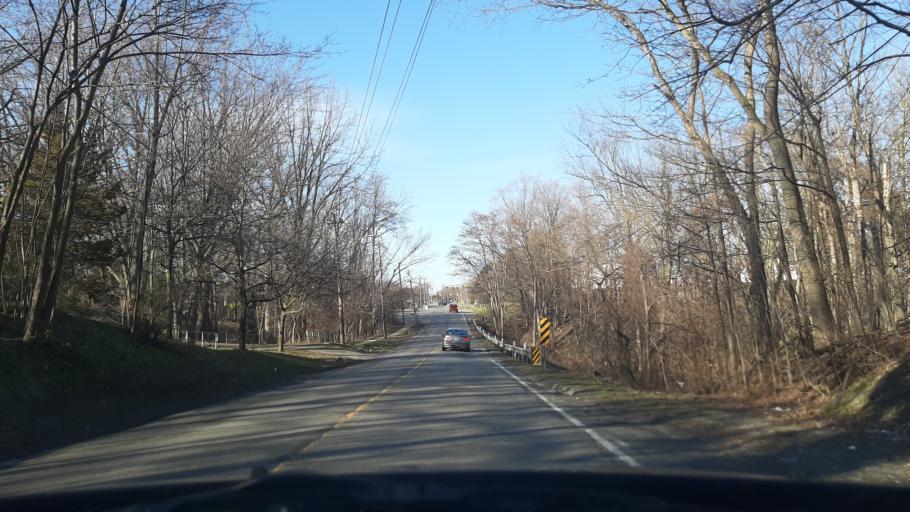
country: CA
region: Ontario
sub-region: Regional Municipality of Niagara
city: St. Catharines
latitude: 43.1872
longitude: -79.2639
